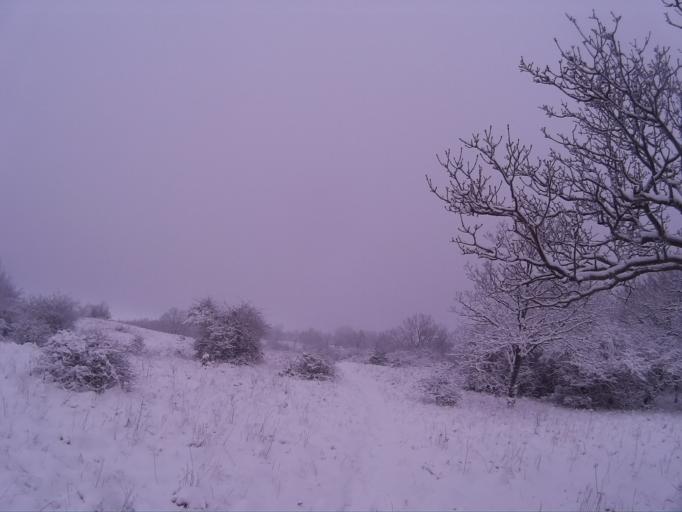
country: HU
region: Komarom-Esztergom
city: Tarjan
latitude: 47.5701
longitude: 18.5325
